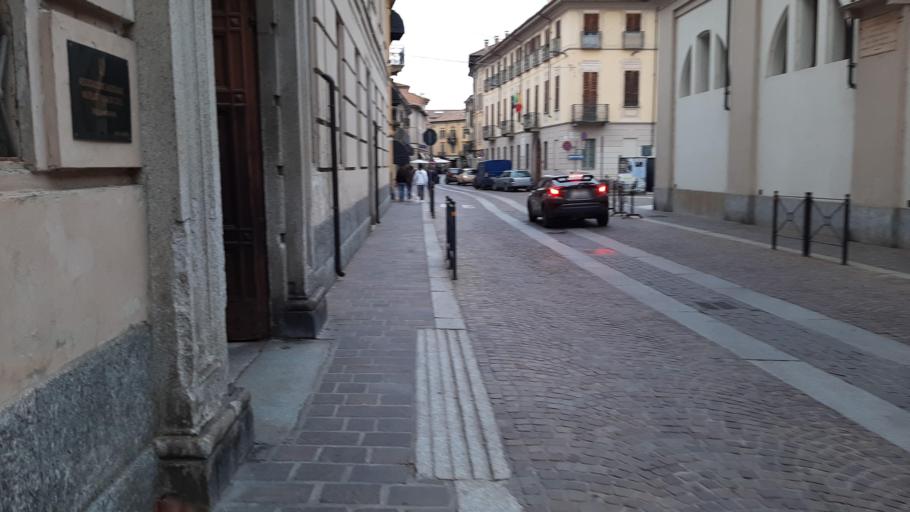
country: IT
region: Lombardy
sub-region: Provincia di Pavia
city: Voghera
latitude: 44.9922
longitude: 9.0056
